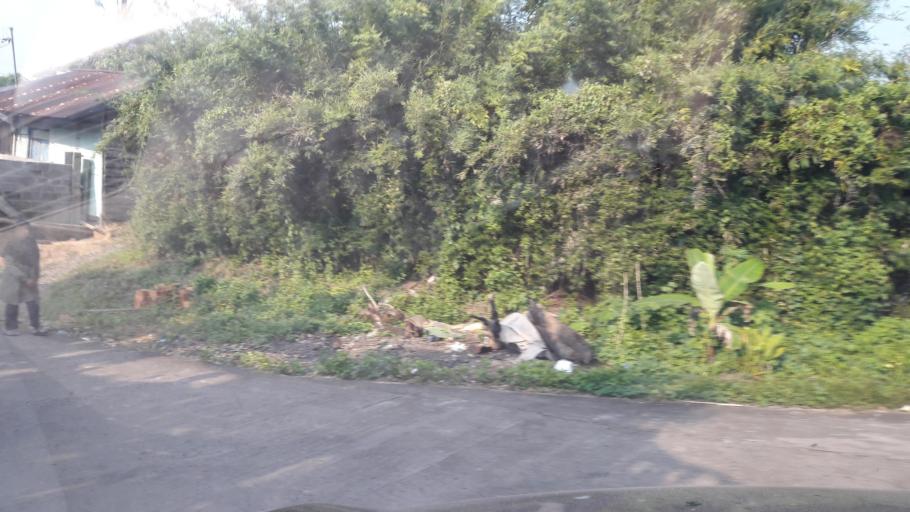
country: ID
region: South Sumatra
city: Gunungmegang Dalam
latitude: -3.2659
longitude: 103.8167
